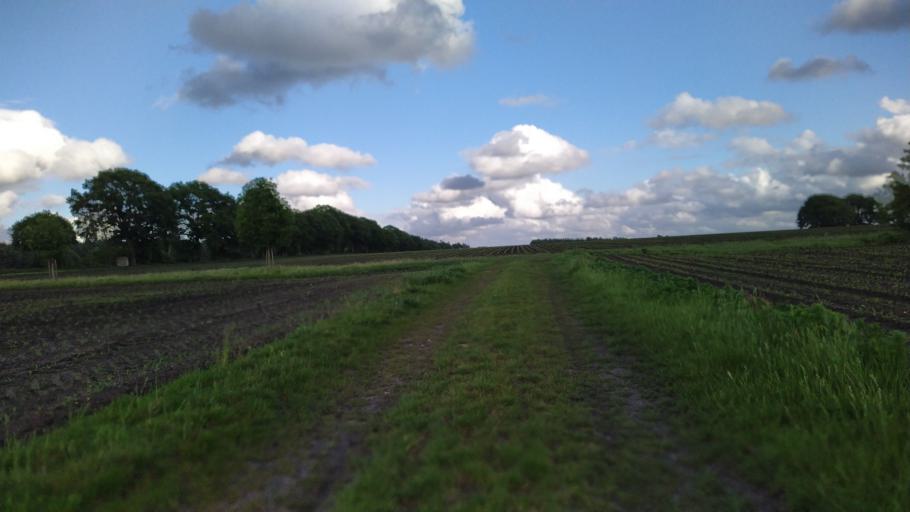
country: DE
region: Lower Saxony
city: Farven
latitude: 53.4526
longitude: 9.2971
